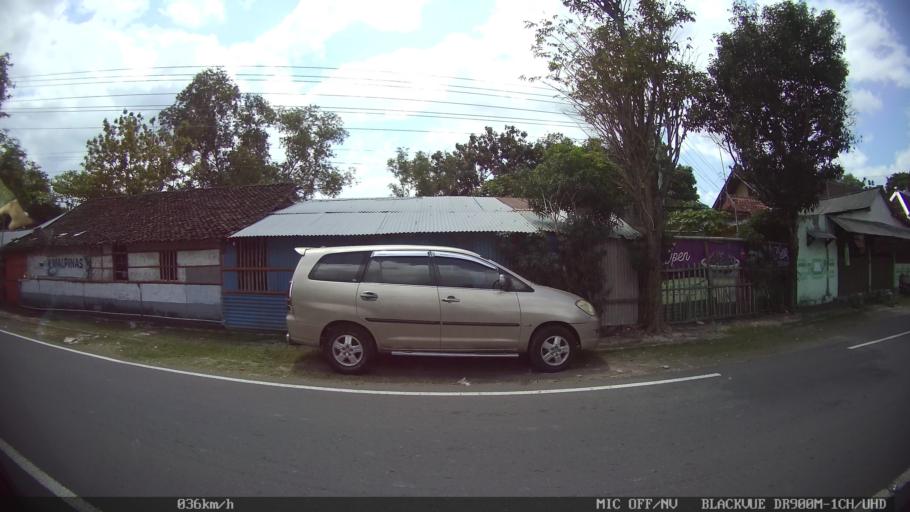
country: ID
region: Daerah Istimewa Yogyakarta
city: Bantul
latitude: -7.8821
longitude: 110.3324
